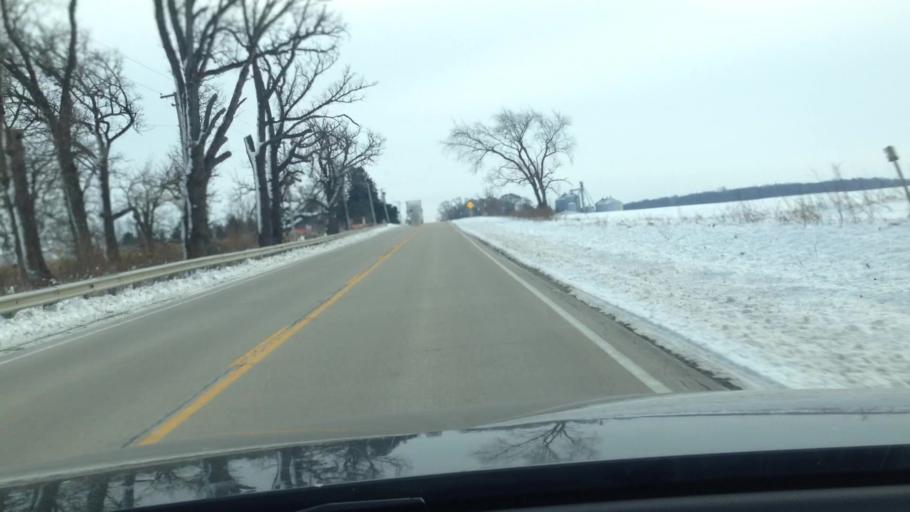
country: US
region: Illinois
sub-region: McHenry County
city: Hebron
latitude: 42.4059
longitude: -88.4382
